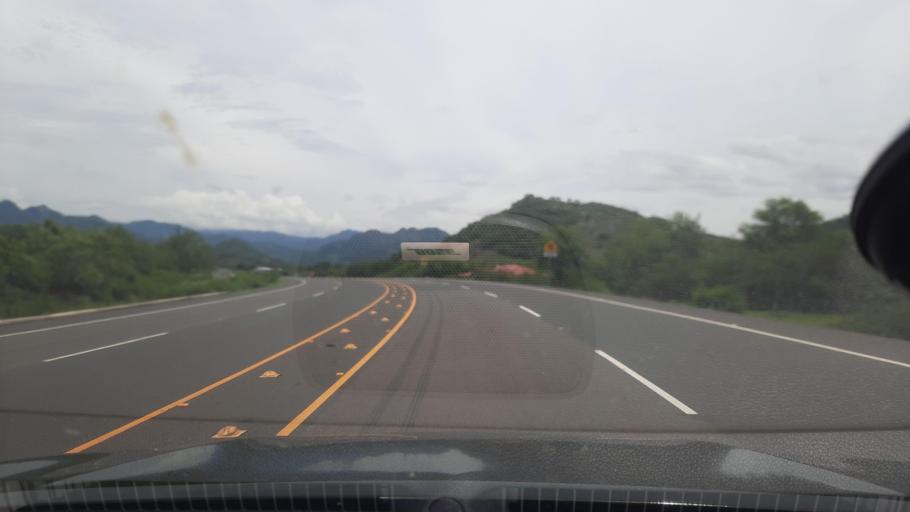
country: HN
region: Valle
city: Aramecina
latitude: 13.7878
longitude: -87.6991
